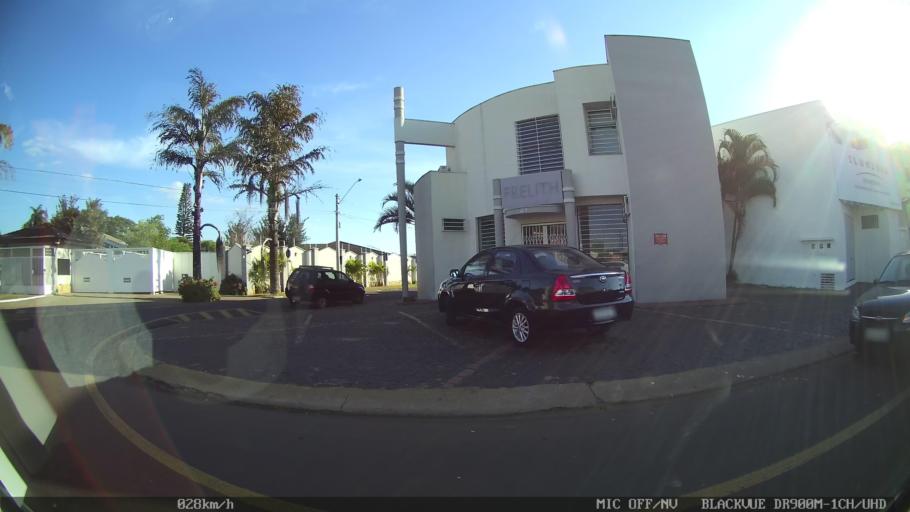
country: BR
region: Sao Paulo
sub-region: Franca
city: Franca
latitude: -20.5183
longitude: -47.3716
